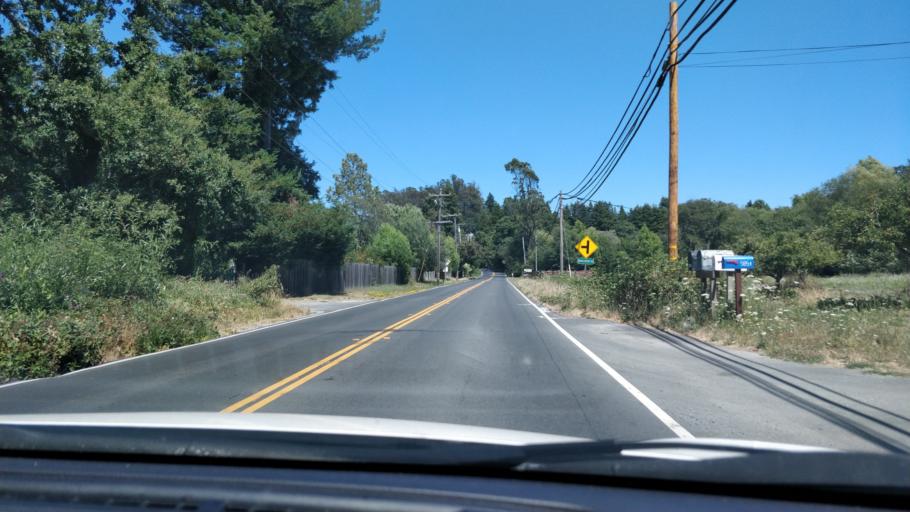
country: US
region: California
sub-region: Sonoma County
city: Graton
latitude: 38.3948
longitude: -122.8714
